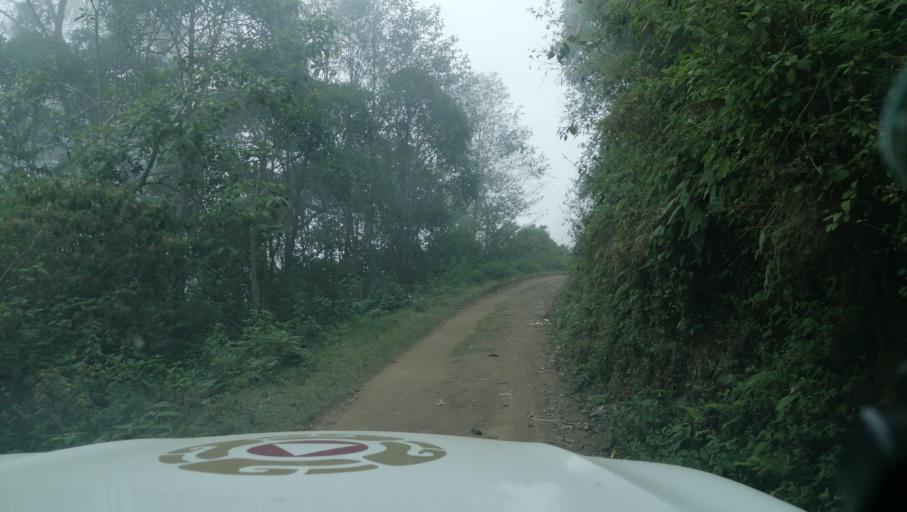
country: GT
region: San Marcos
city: Tacana
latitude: 15.2146
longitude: -92.1834
